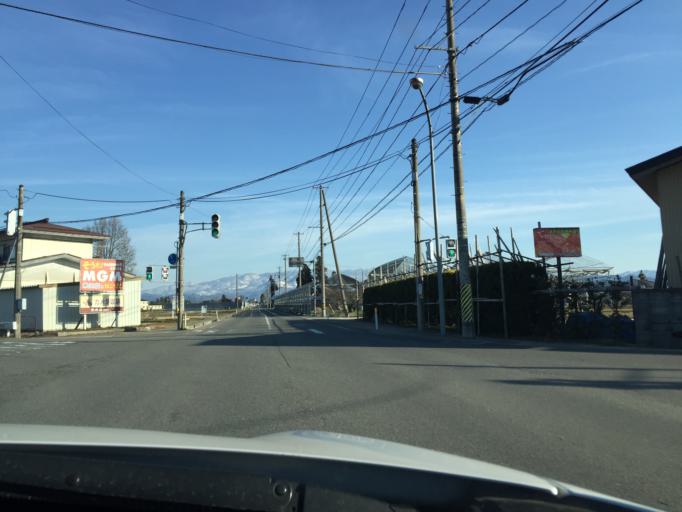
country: JP
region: Yamagata
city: Yonezawa
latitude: 37.9743
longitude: 140.0869
